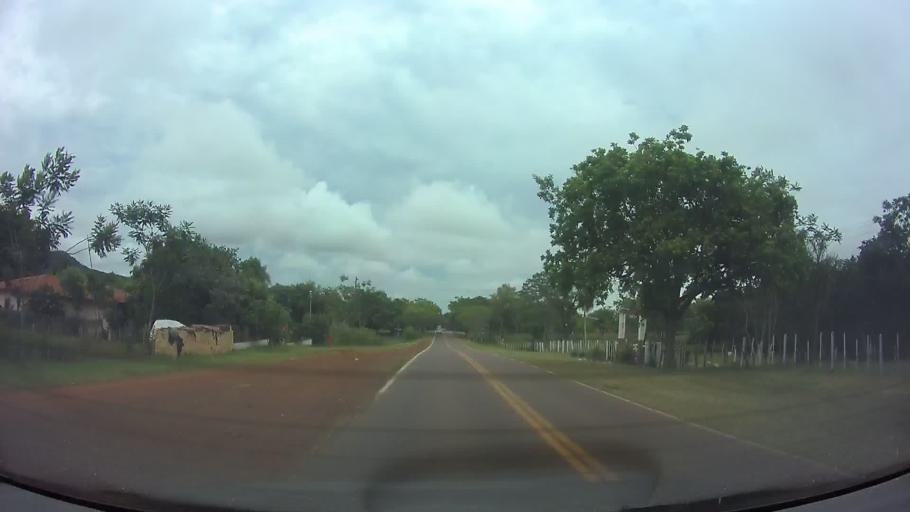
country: PY
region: Paraguari
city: Carapegua
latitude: -25.7957
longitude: -57.2027
